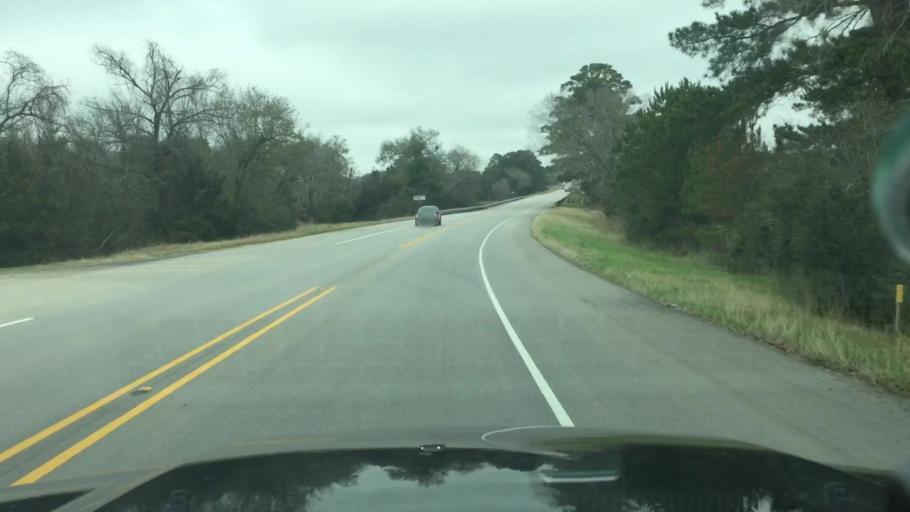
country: US
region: Texas
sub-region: Lee County
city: Giddings
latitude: 30.0826
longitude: -96.9170
